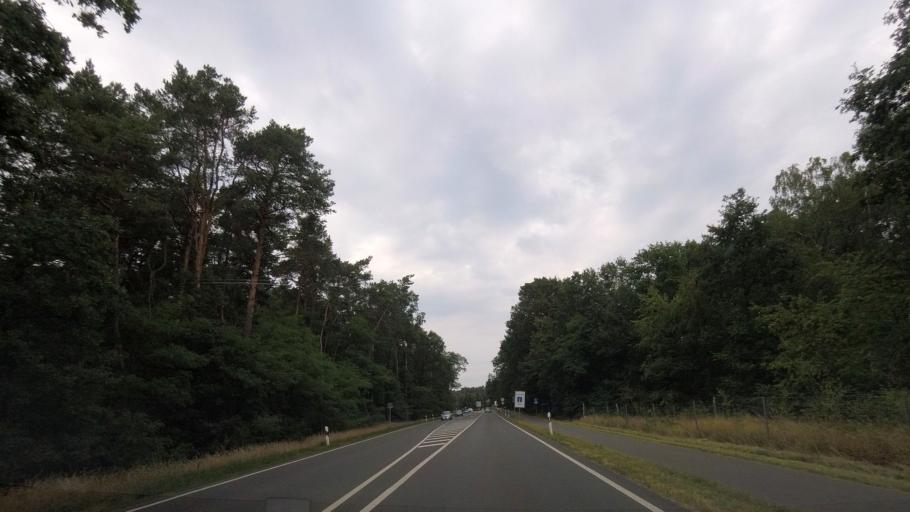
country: DE
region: Brandenburg
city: Michendorf
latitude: 52.2936
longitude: 13.0225
